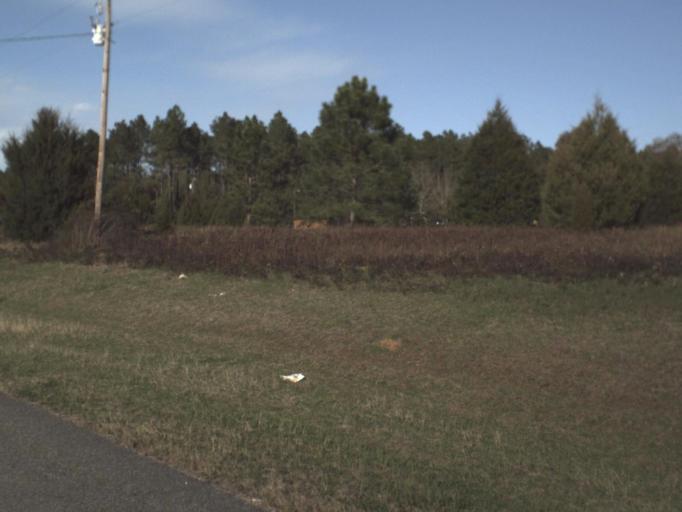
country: US
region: Florida
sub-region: Jackson County
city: Marianna
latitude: 30.5849
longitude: -85.1820
